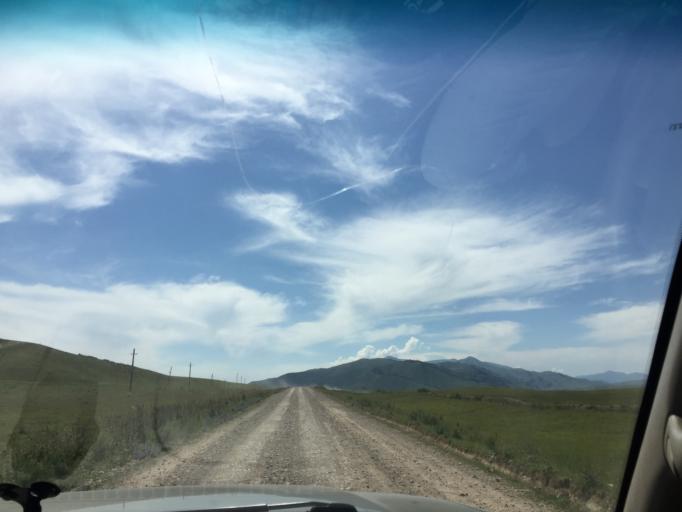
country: KZ
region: Almaty Oblysy
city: Kegen
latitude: 42.7690
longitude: 79.0927
